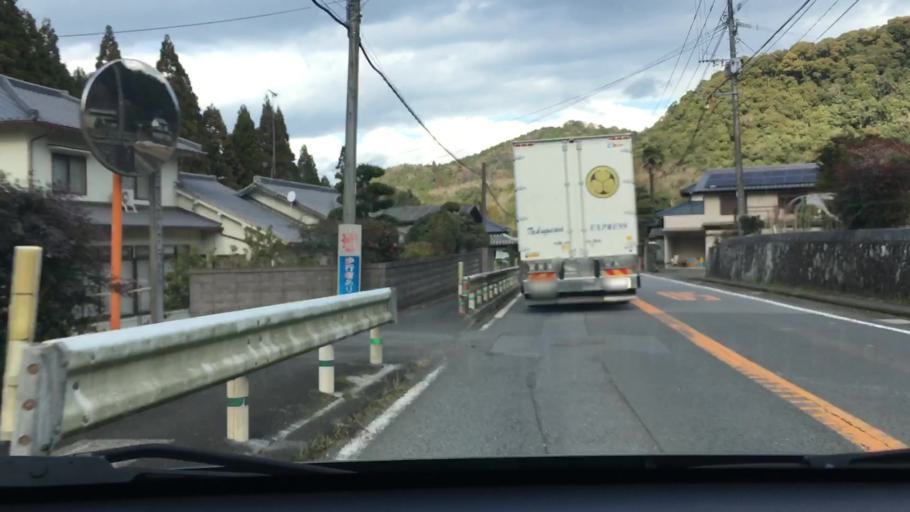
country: JP
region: Oita
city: Usuki
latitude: 33.0152
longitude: 131.7006
